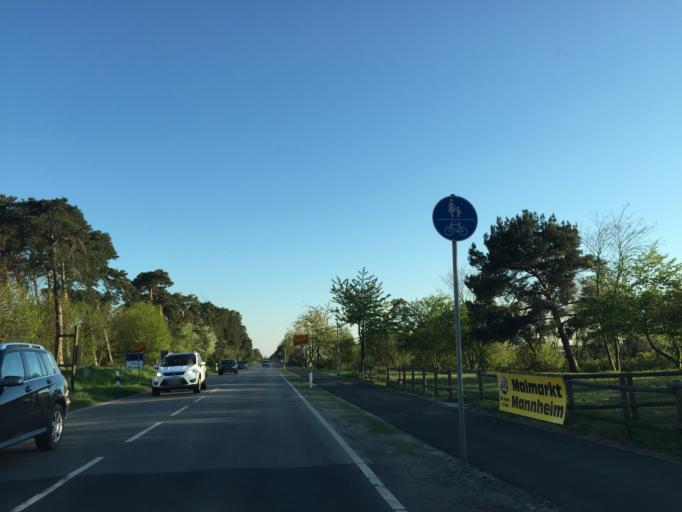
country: DE
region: Hesse
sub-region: Regierungsbezirk Darmstadt
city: Bickenbach
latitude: 49.7501
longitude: 8.6102
